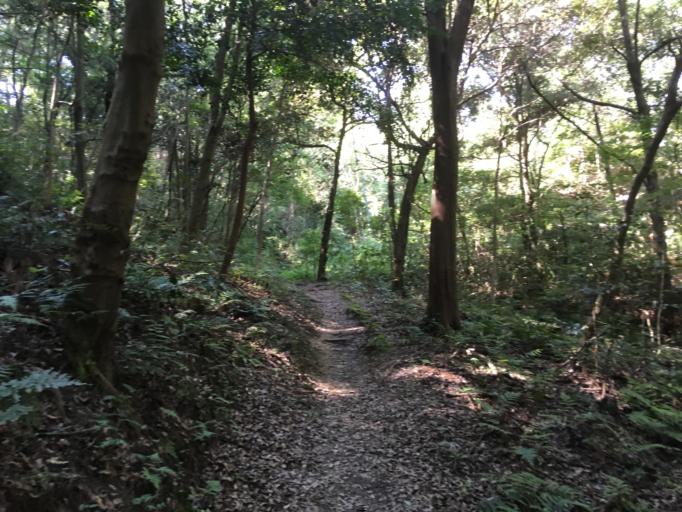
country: JP
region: Osaka
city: Neyagawa
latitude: 34.7432
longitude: 135.6837
